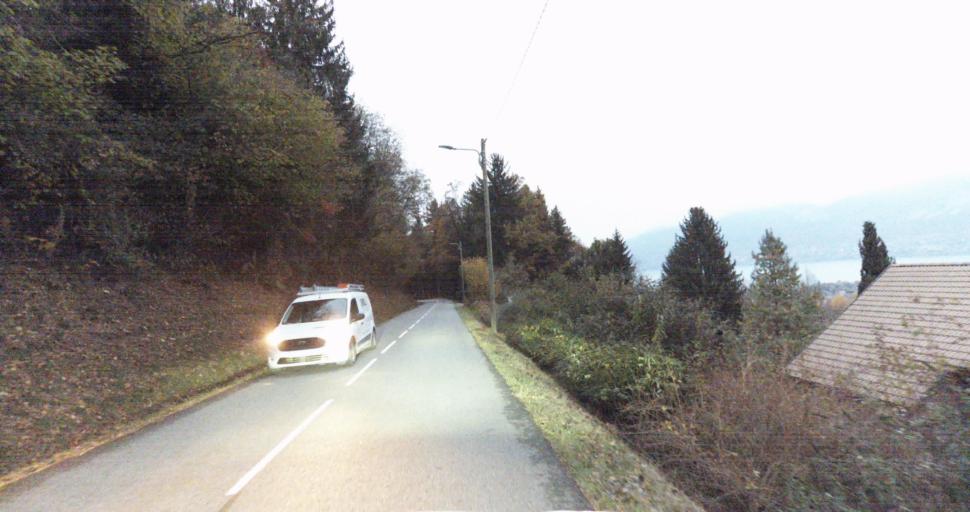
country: FR
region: Rhone-Alpes
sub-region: Departement de la Haute-Savoie
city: Sevrier
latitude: 45.8409
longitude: 6.1398
